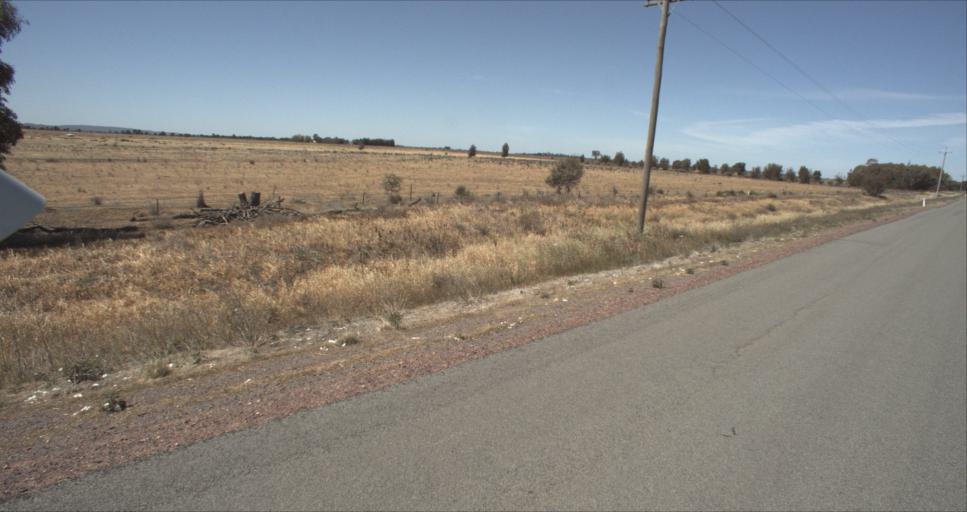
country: AU
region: New South Wales
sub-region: Leeton
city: Leeton
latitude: -34.4328
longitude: 146.2993
